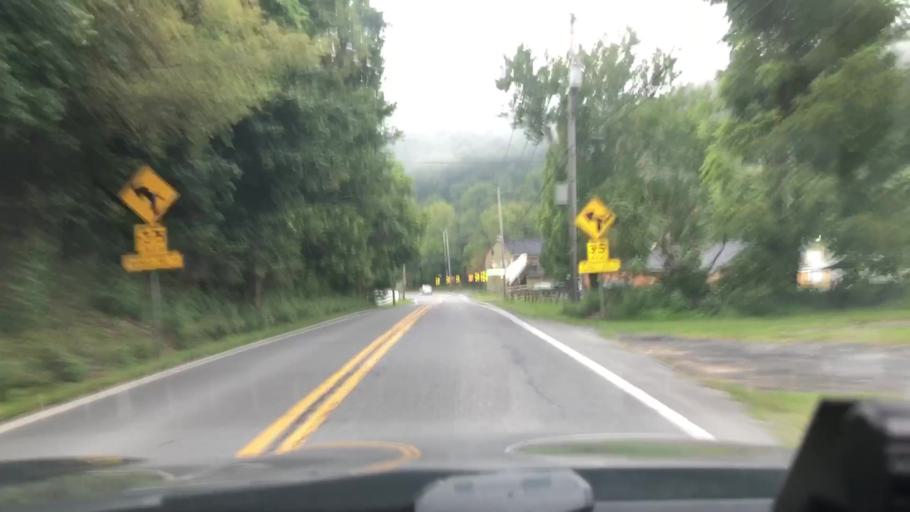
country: US
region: Pennsylvania
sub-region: Berks County
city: Kutztown
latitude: 40.5584
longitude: -75.8080
